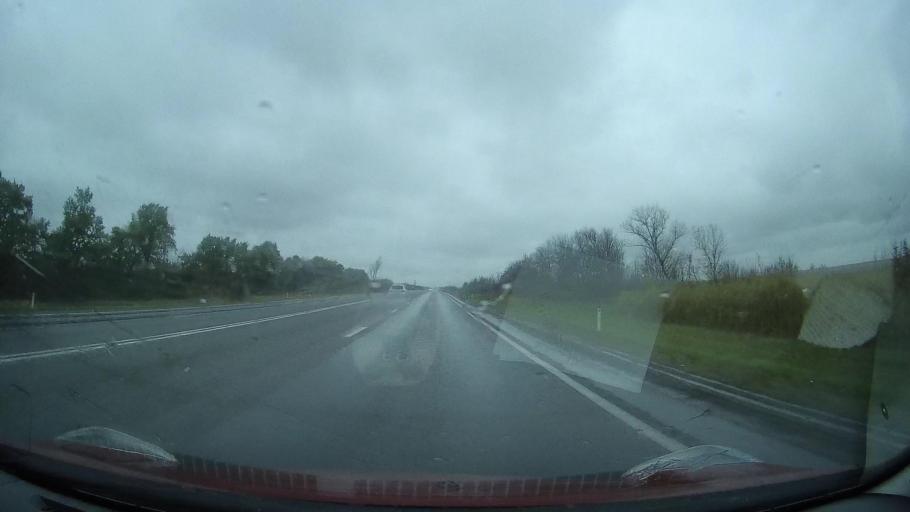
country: RU
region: Stavropol'skiy
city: Nevinnomyssk
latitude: 44.6312
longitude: 42.0249
